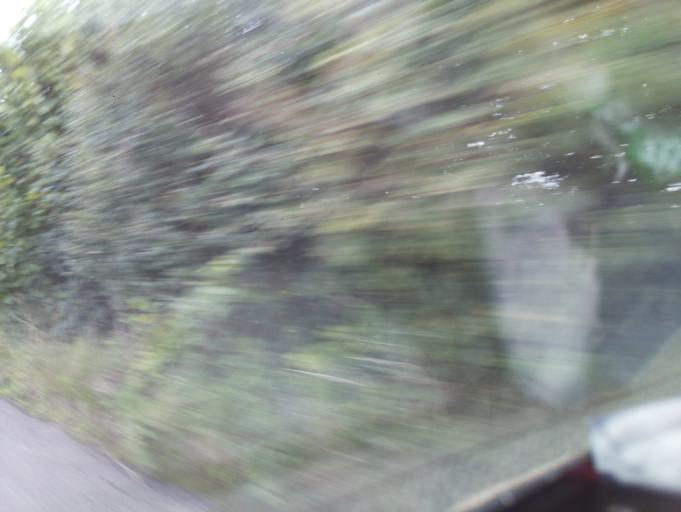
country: GB
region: England
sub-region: Wiltshire
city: Colerne
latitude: 51.4694
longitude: -2.2425
